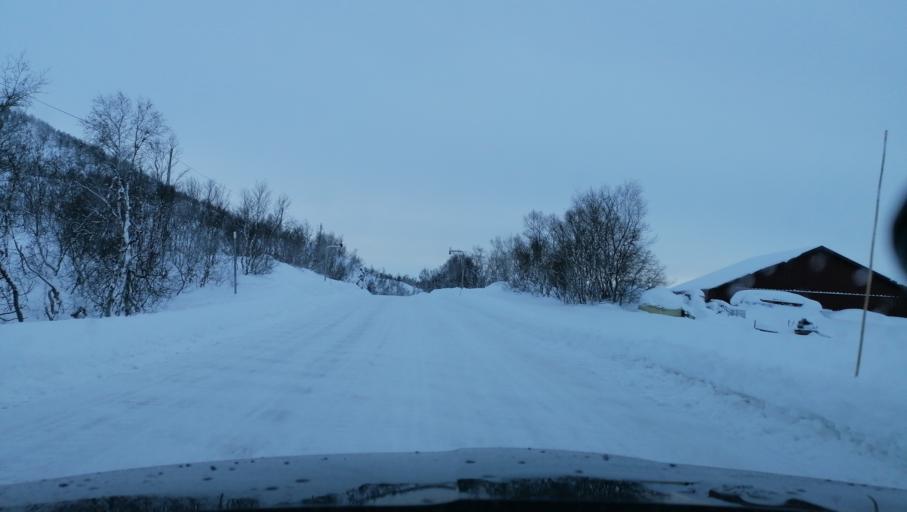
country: NO
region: Aust-Agder
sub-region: Bykle
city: Hovden
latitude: 59.6434
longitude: 7.4589
